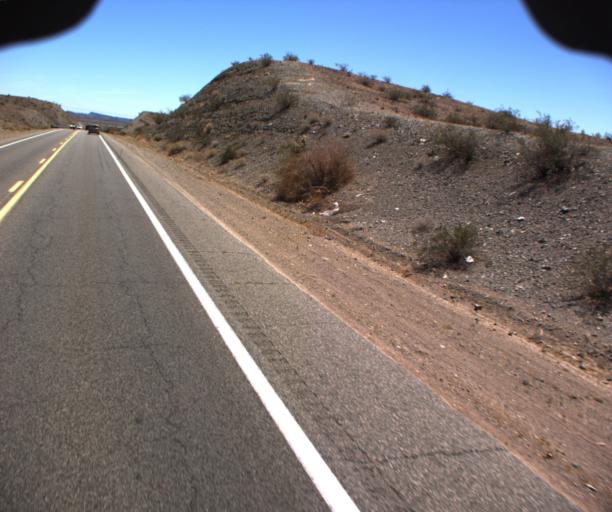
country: US
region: Arizona
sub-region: Mohave County
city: Lake Havasu City
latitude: 34.4295
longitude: -114.2122
